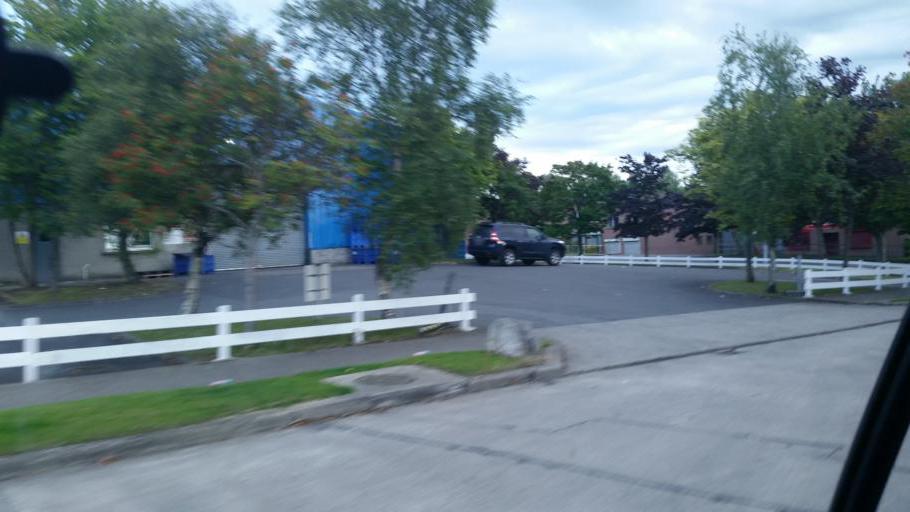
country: IE
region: Leinster
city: Beaumont
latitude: 53.4052
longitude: -6.2373
